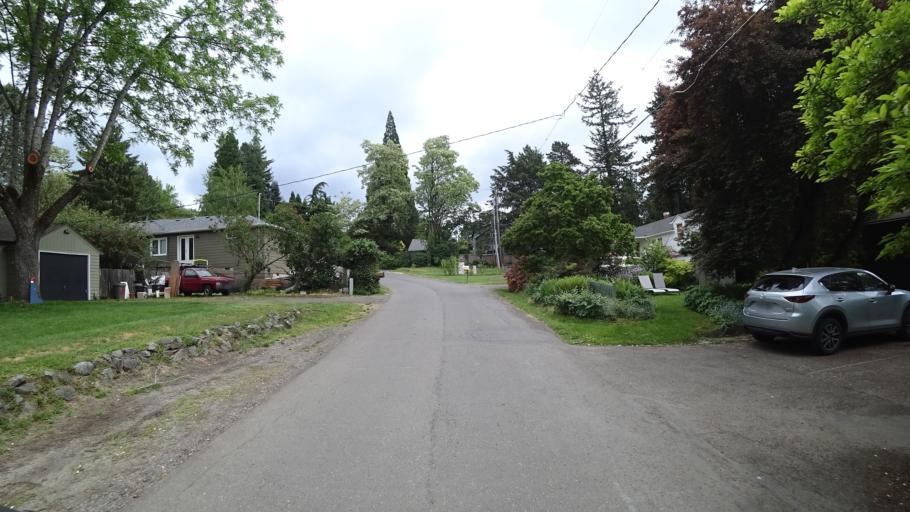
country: US
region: Oregon
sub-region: Washington County
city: Garden Home-Whitford
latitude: 45.4723
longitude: -122.7343
